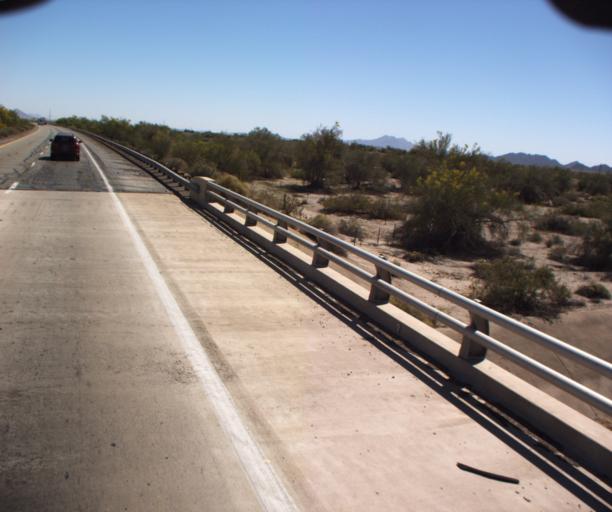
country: US
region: Arizona
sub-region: Yuma County
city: Wellton
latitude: 32.6490
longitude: -114.2103
